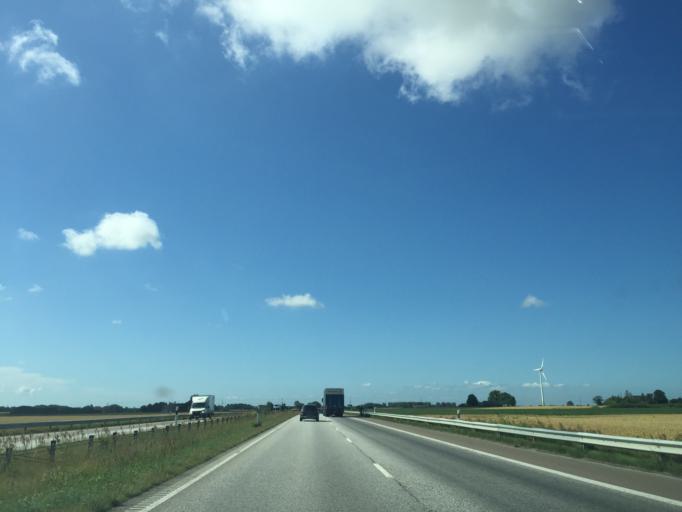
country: SE
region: Skane
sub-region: Angelholms Kommun
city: AEngelholm
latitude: 56.2173
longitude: 12.8919
